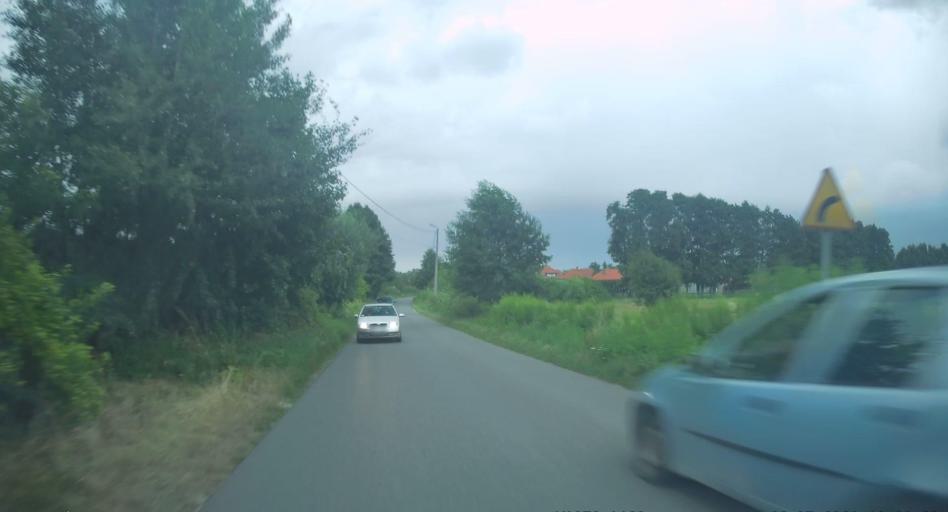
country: PL
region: Lodz Voivodeship
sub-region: Powiat rawski
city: Rawa Mazowiecka
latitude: 51.7494
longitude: 20.2140
